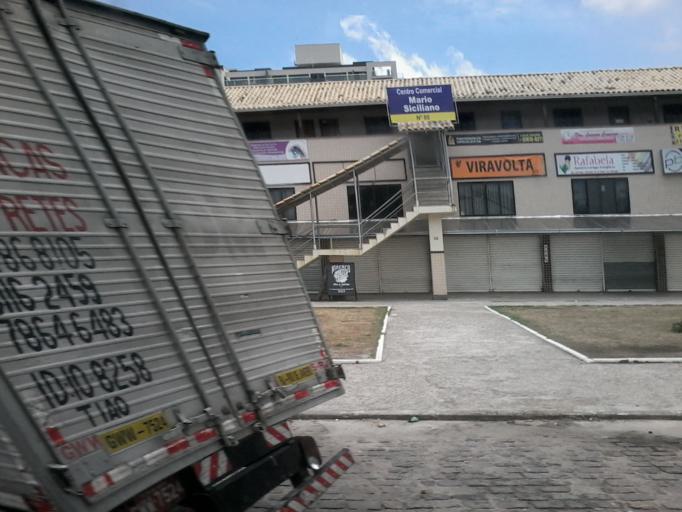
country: BR
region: Rio de Janeiro
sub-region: Nilopolis
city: Nilopolis
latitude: -23.0236
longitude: -43.4820
